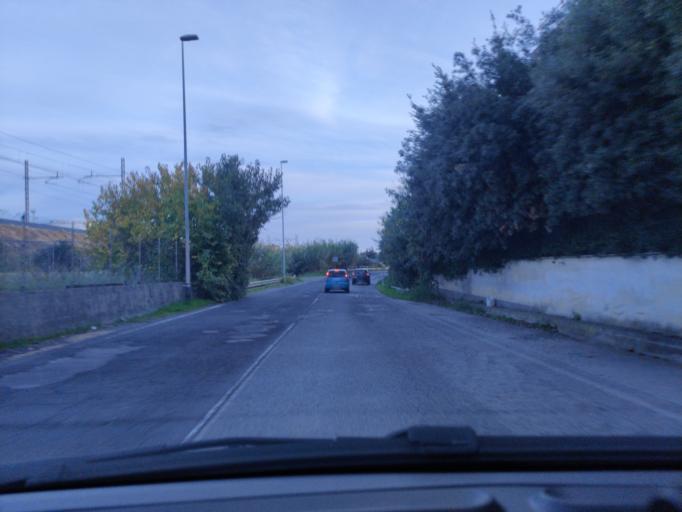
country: IT
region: Latium
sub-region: Citta metropolitana di Roma Capitale
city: Civitavecchia
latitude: 42.1121
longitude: 11.7761
